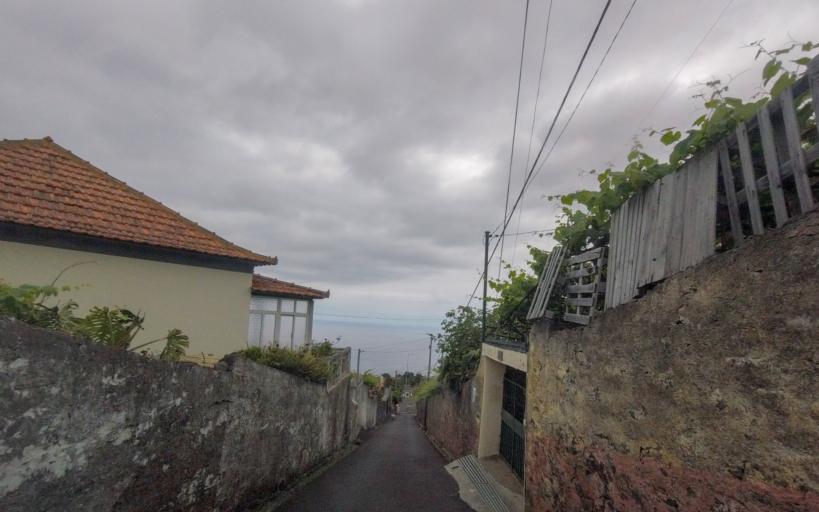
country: PT
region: Madeira
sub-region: Funchal
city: Nossa Senhora do Monte
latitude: 32.6567
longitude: -16.8821
